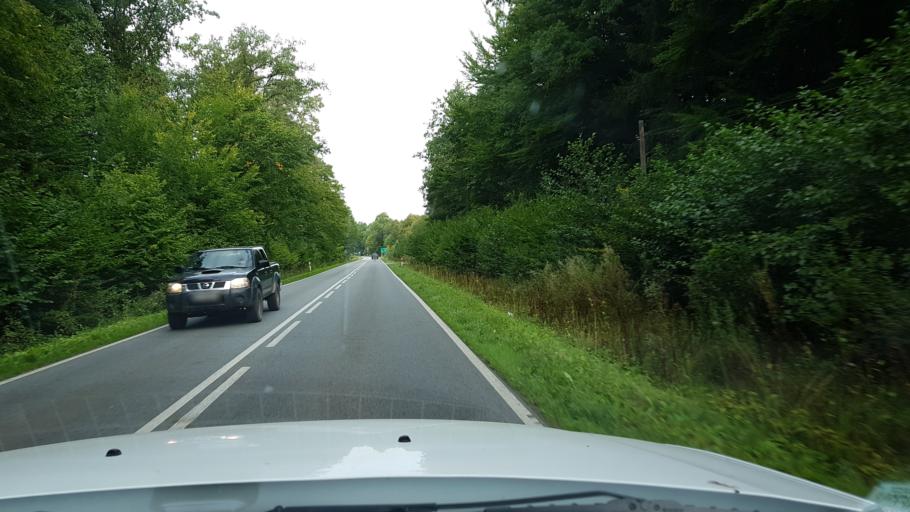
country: PL
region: West Pomeranian Voivodeship
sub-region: Powiat slawienski
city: Slawno
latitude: 54.3832
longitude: 16.6180
